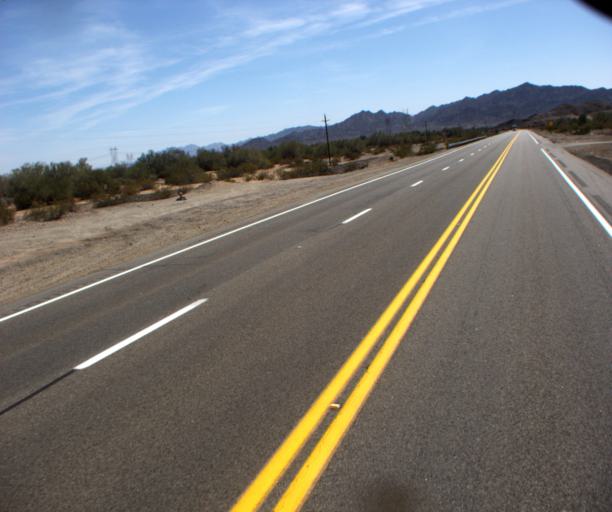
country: US
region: Arizona
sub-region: Yuma County
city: Fortuna Foothills
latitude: 32.7983
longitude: -114.3810
